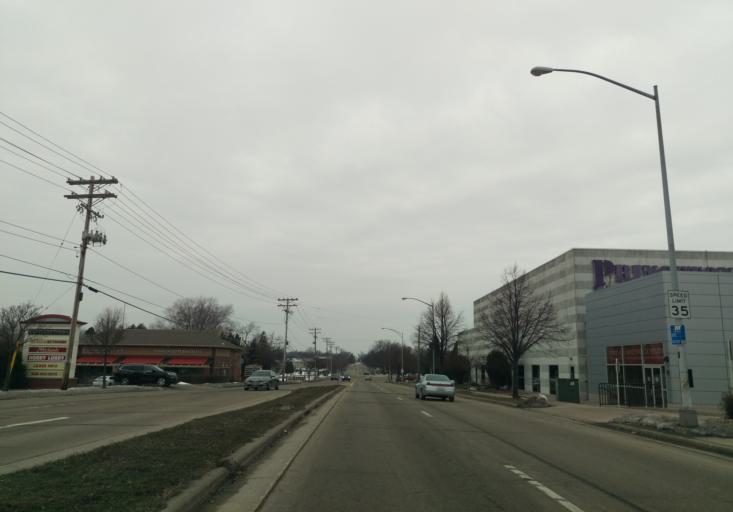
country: US
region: Wisconsin
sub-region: Dane County
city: Monona
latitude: 43.1211
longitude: -89.3078
